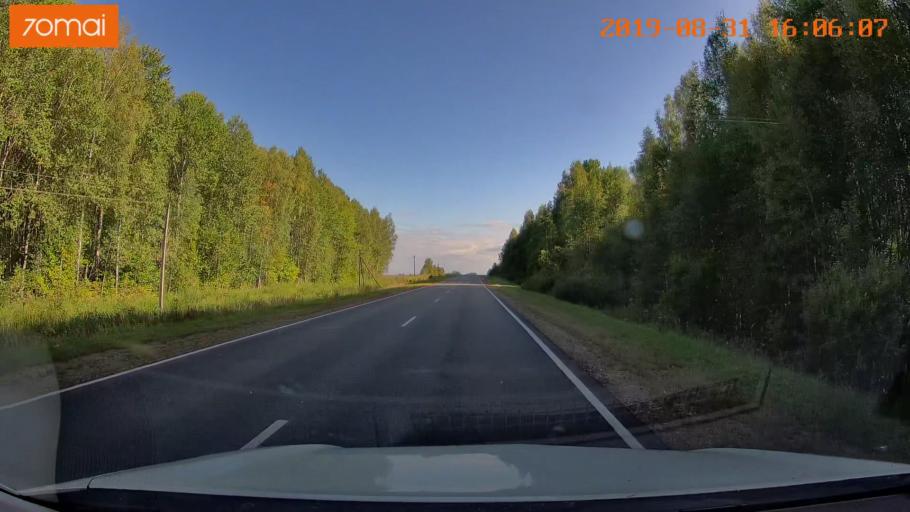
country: RU
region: Kaluga
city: Yukhnov
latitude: 54.6290
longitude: 35.3426
